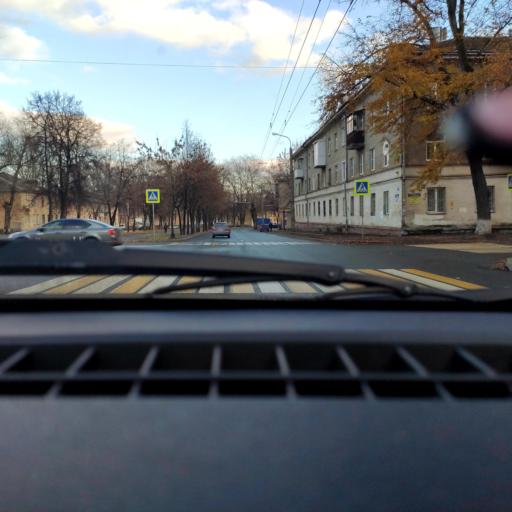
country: RU
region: Bashkortostan
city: Ufa
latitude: 54.8209
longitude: 56.0978
